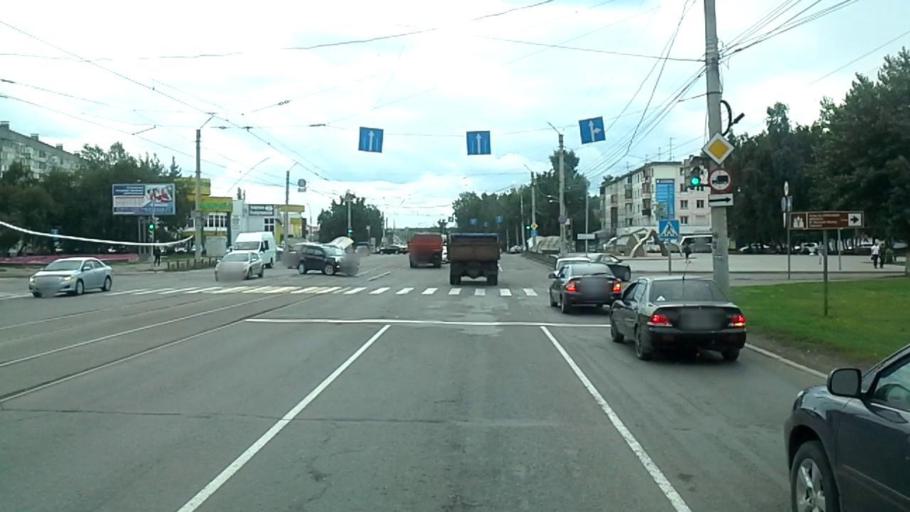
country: RU
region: Altai Krai
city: Biysk
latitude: 52.5420
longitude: 85.2190
